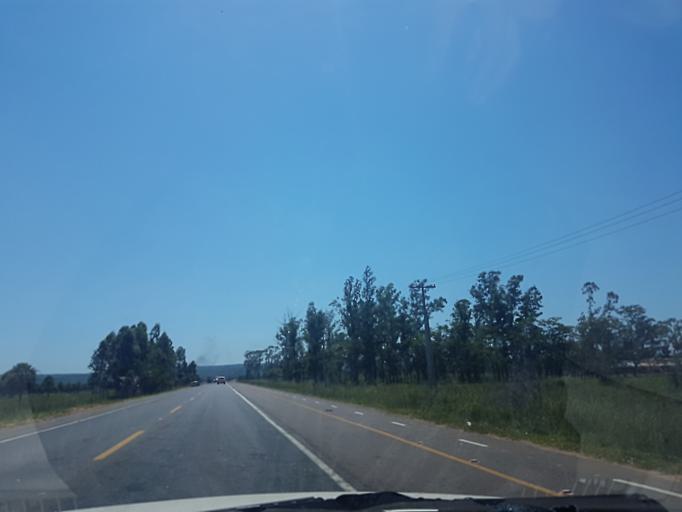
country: PY
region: Cordillera
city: Emboscada
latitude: -25.2085
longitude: -57.3892
